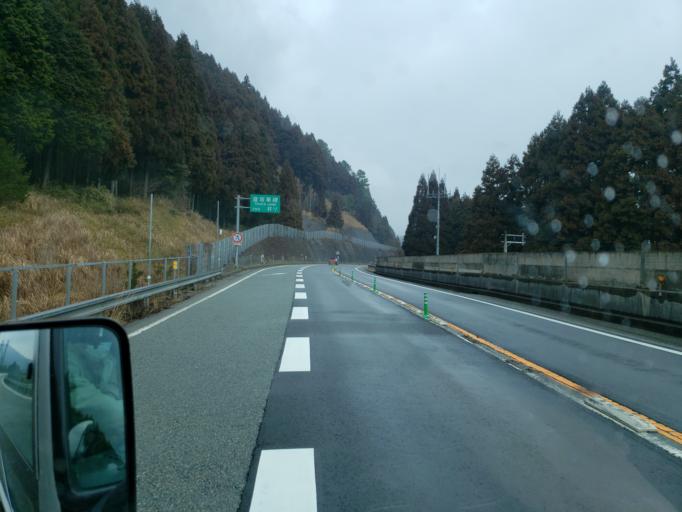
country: JP
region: Hyogo
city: Nishiwaki
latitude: 35.1247
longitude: 134.7874
